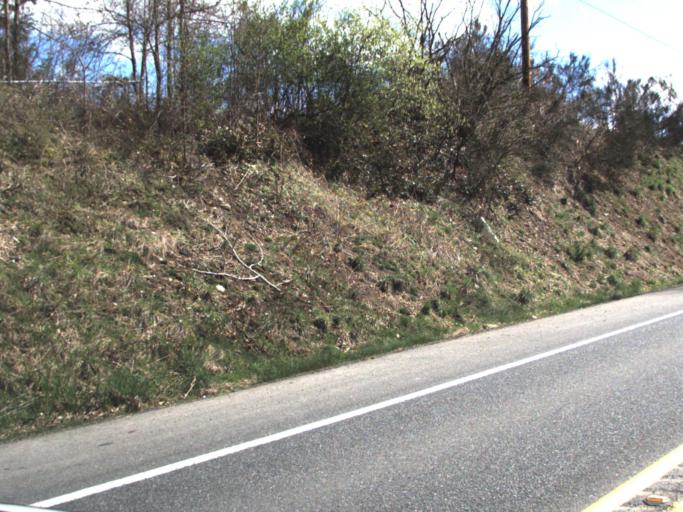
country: US
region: Washington
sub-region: King County
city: Enumclaw
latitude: 47.2086
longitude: -122.0195
